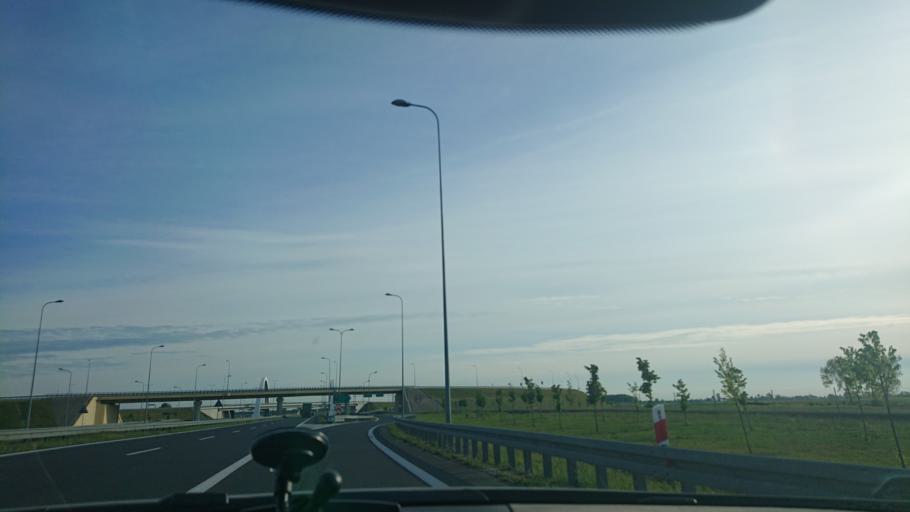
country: PL
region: Greater Poland Voivodeship
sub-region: Powiat gnieznienski
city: Lubowo
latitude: 52.5247
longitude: 17.5088
